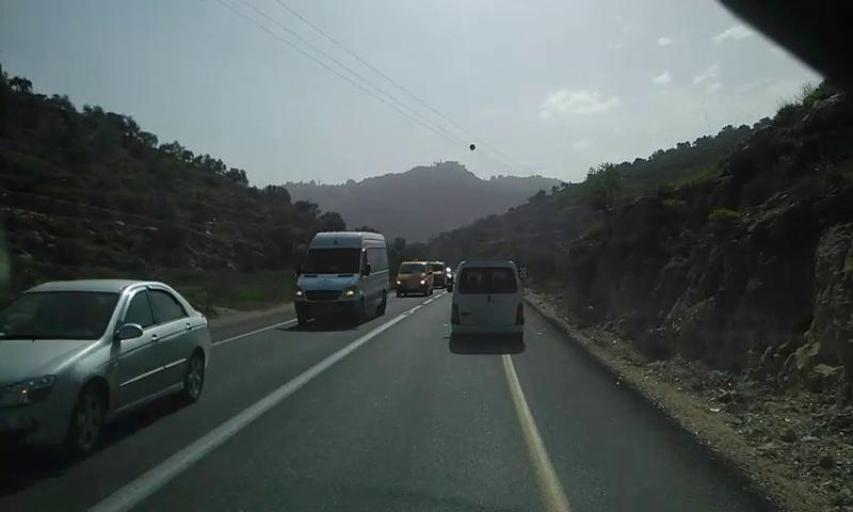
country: PS
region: West Bank
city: Silwad
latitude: 31.9945
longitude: 35.2448
